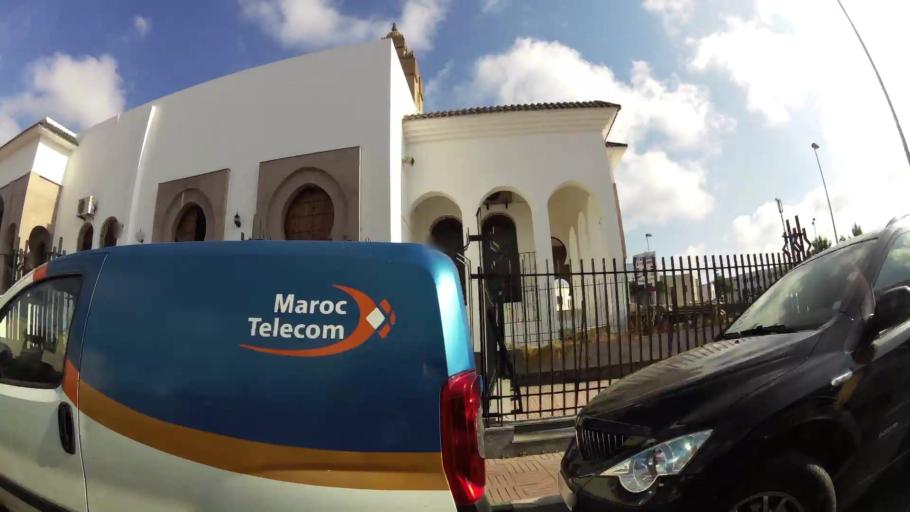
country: MA
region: Rabat-Sale-Zemmour-Zaer
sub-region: Skhirate-Temara
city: Temara
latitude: 33.9535
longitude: -6.8711
